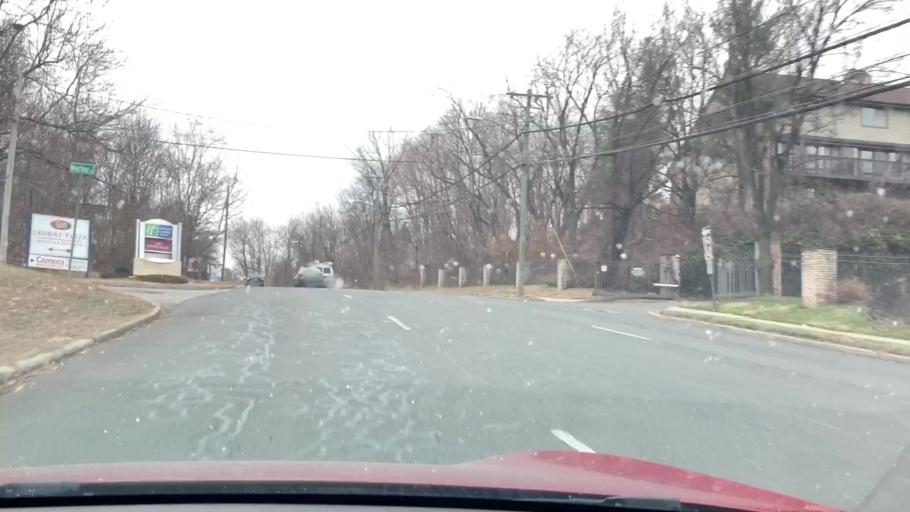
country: US
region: Connecticut
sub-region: Fairfield County
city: Stamford
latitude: 41.0698
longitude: -73.5458
